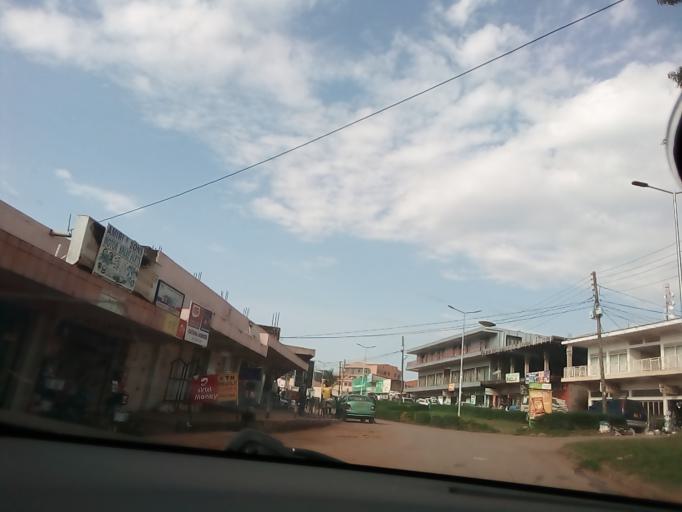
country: UG
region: Central Region
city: Masaka
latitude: -0.3405
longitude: 31.7388
